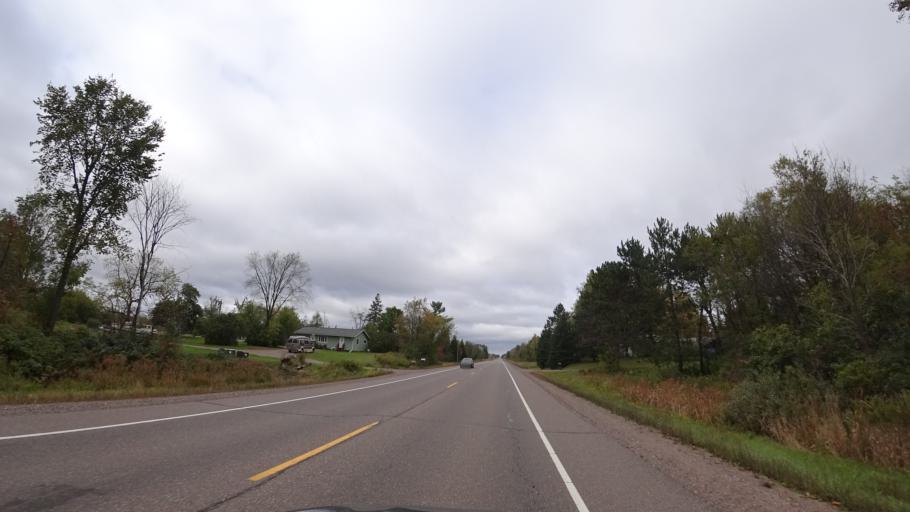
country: US
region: Wisconsin
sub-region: Rusk County
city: Ladysmith
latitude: 45.4845
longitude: -91.1114
